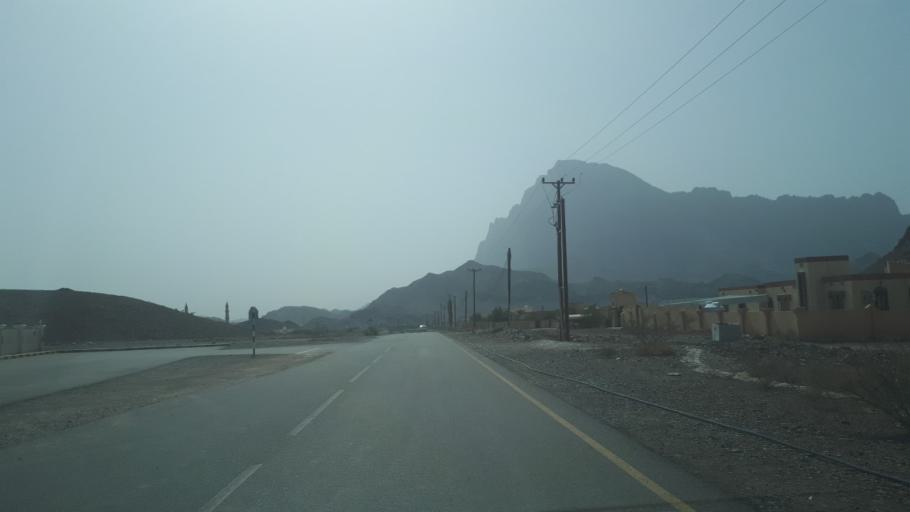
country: OM
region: Muhafazat ad Dakhiliyah
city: Bahla'
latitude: 23.2264
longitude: 57.0557
